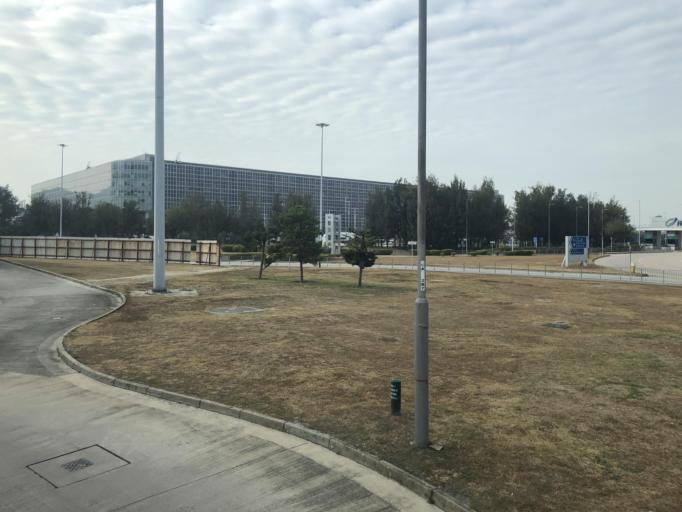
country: HK
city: Tai O
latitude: 22.2980
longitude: 113.9329
